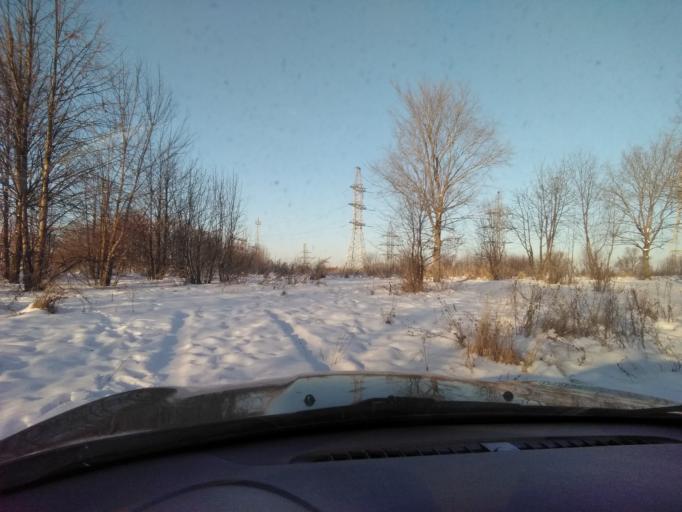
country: RU
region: Tatarstan
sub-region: Gorod Kazan'
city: Kazan
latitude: 55.8357
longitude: 49.1669
